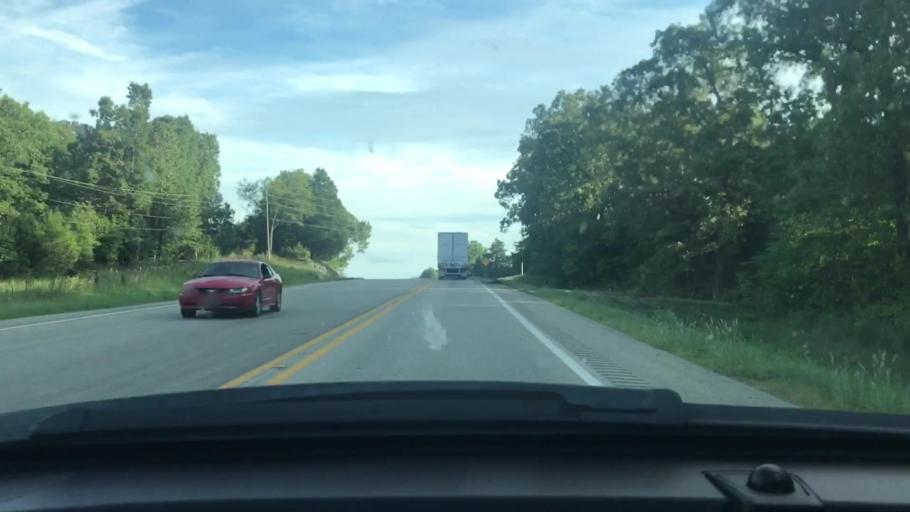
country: US
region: Arkansas
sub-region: Lawrence County
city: Hoxie
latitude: 36.1565
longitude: -91.1618
